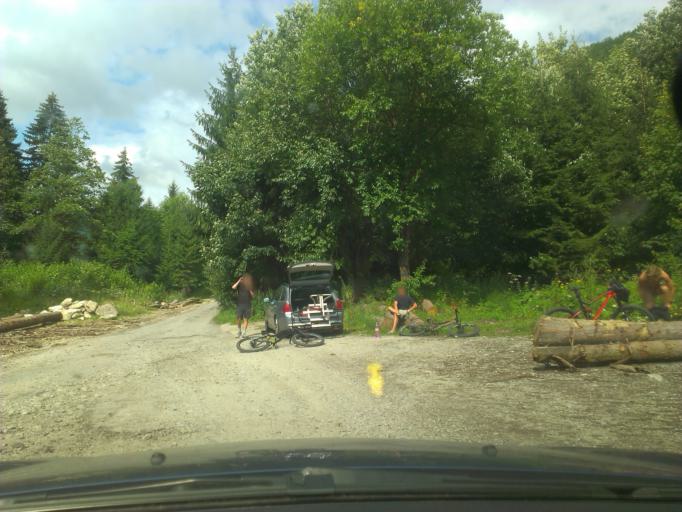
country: SK
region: Zilinsky
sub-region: Okres Zilina
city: Vrutky
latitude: 49.1032
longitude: 18.8850
